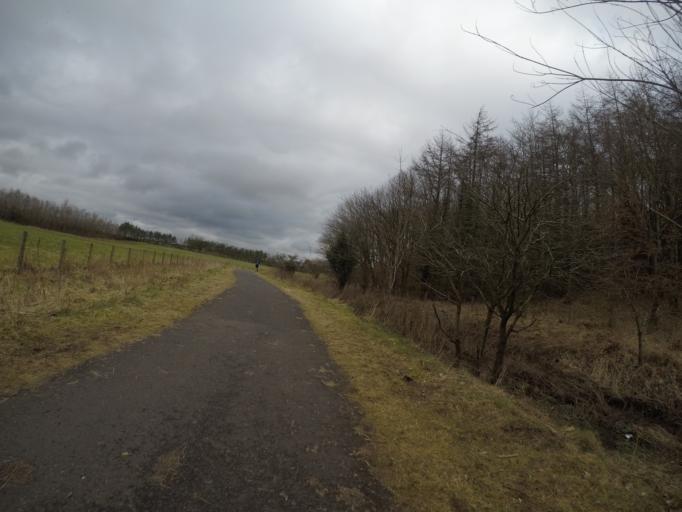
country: GB
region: Scotland
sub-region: North Ayrshire
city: Springside
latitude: 55.6129
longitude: -4.6091
